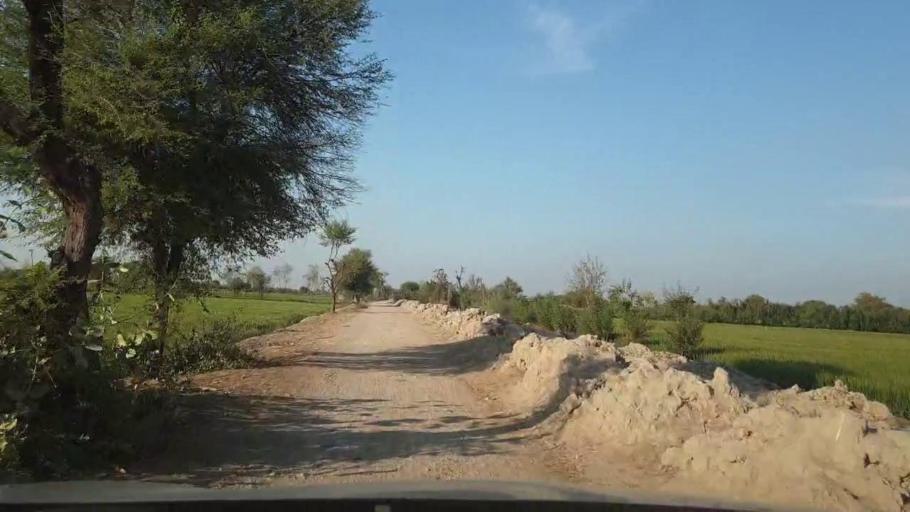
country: PK
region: Sindh
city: Tando Adam
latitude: 25.6941
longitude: 68.7023
